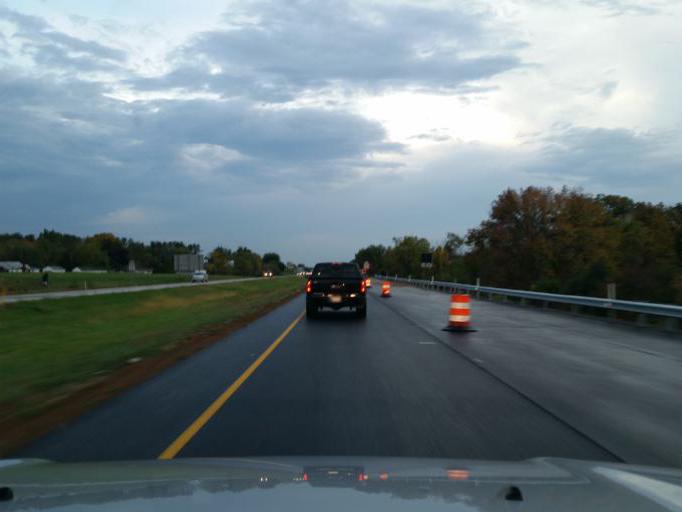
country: US
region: Maryland
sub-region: Frederick County
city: Emmitsburg
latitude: 39.7226
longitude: -77.3055
